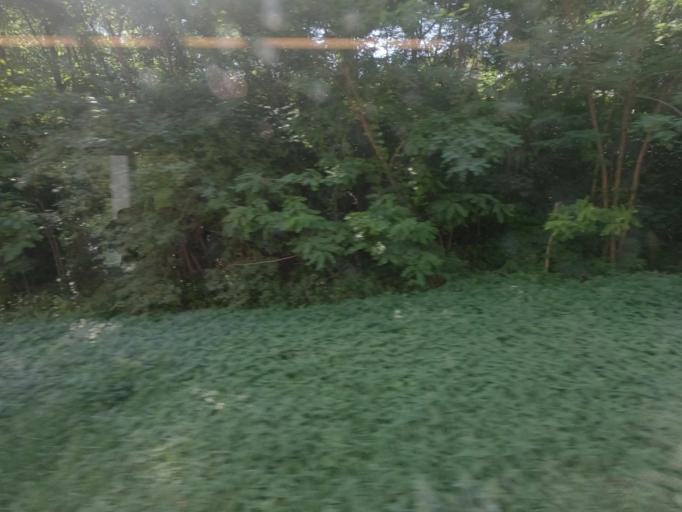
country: CH
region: Valais
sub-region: Martigny District
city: Martigny-Combe
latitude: 46.0778
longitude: 7.0753
